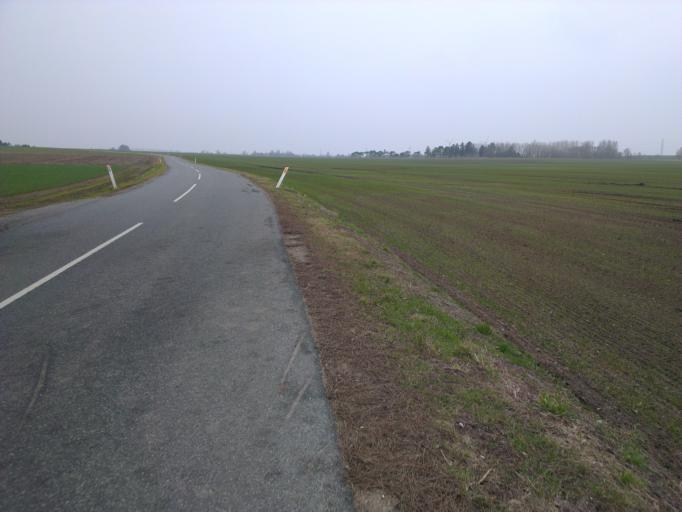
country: DK
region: Capital Region
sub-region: Frederikssund Kommune
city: Skibby
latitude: 55.7875
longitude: 11.9991
